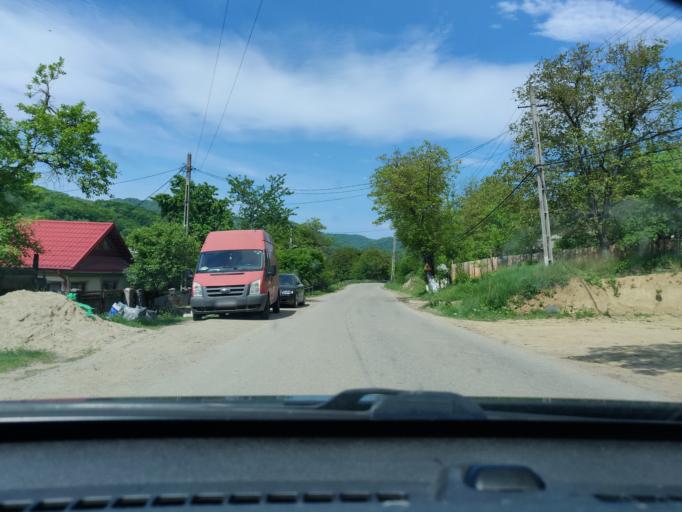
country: RO
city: Vizantea-Manastireasca
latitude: 45.9604
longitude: 26.8248
